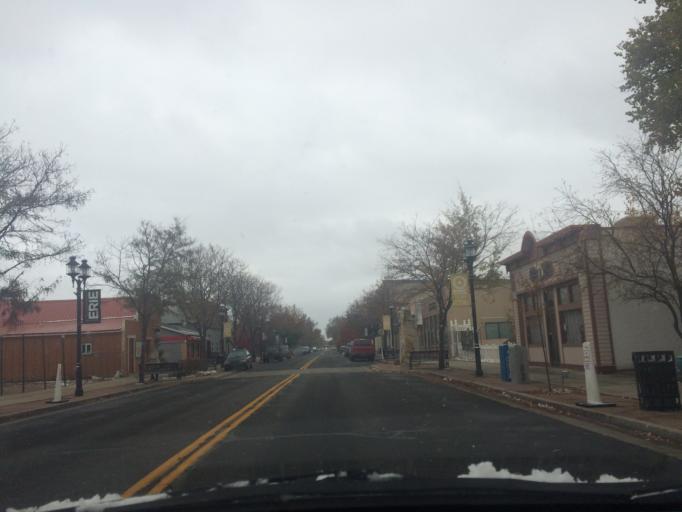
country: US
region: Colorado
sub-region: Boulder County
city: Erie
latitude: 40.0499
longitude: -105.0475
